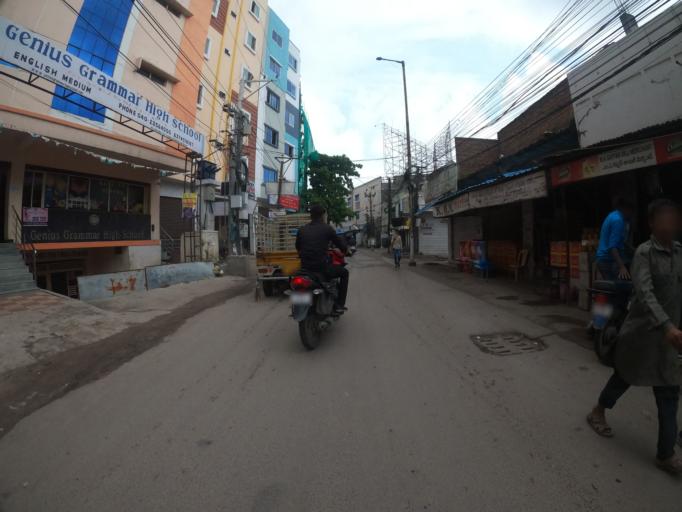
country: IN
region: Telangana
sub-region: Hyderabad
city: Hyderabad
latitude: 17.3977
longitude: 78.4172
